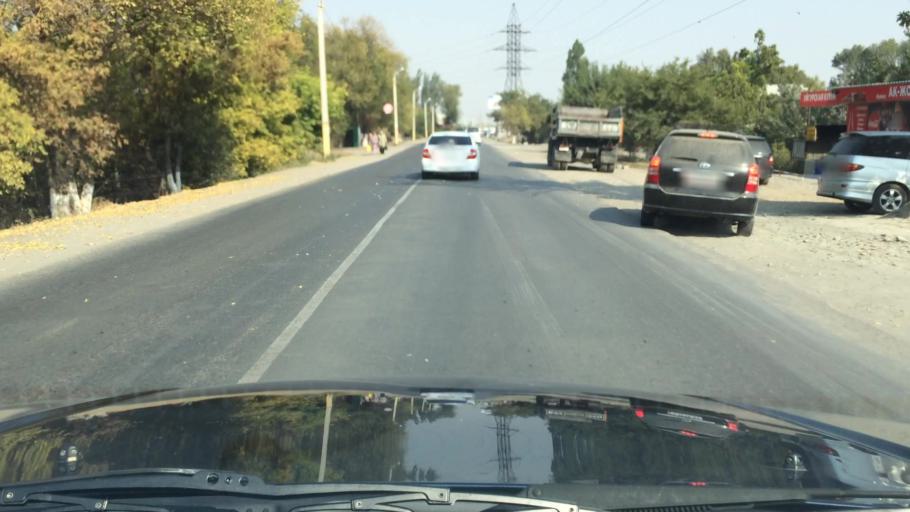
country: KG
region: Chuy
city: Lebedinovka
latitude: 42.8868
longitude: 74.6787
